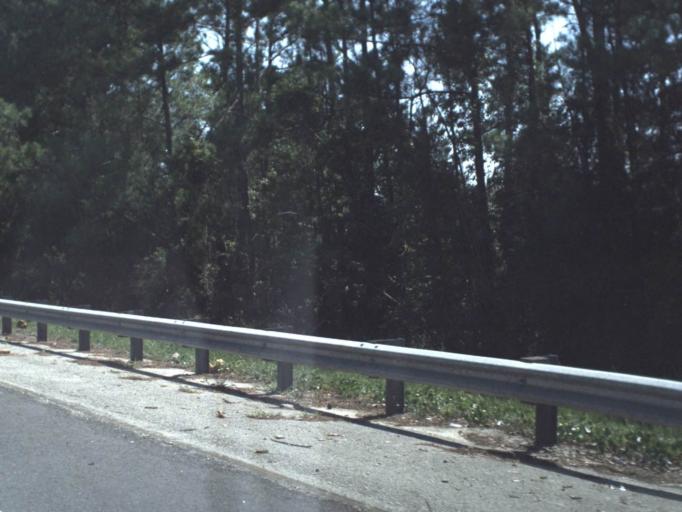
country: US
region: Florida
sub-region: Nassau County
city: Yulee
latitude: 30.5919
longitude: -81.5997
